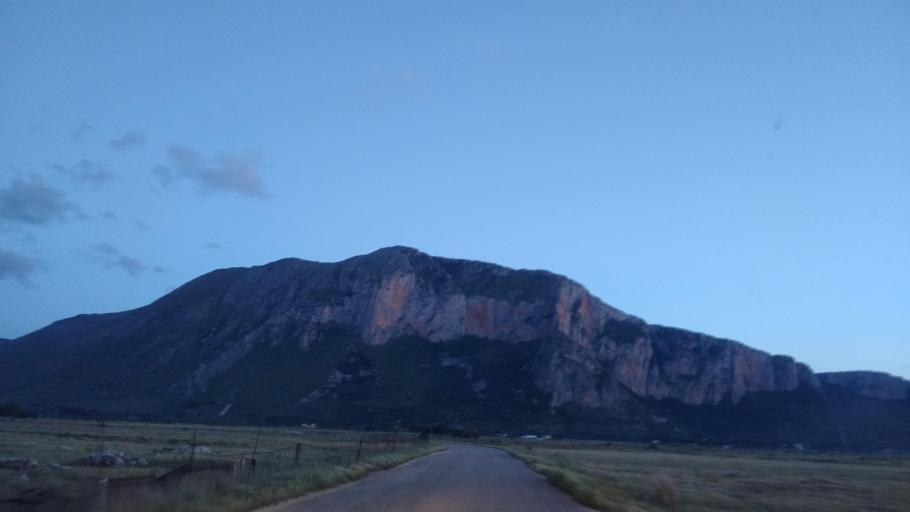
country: IT
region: Sicily
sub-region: Trapani
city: Castelluzzo
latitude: 38.1154
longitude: 12.7204
